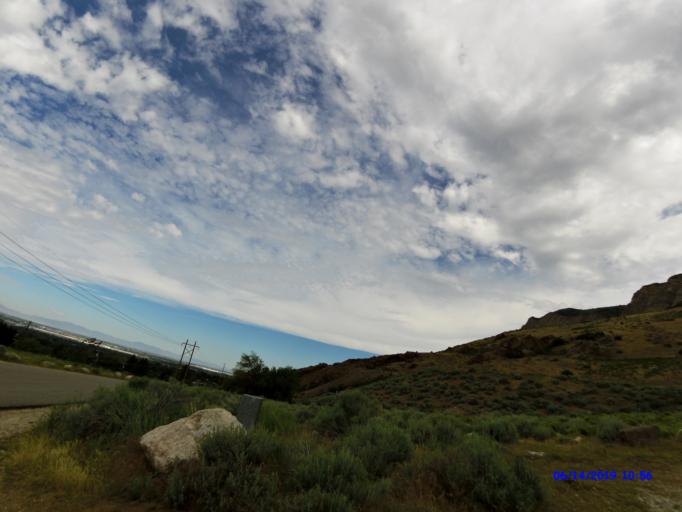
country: US
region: Utah
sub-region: Weber County
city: Ogden
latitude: 41.2476
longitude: -111.9339
